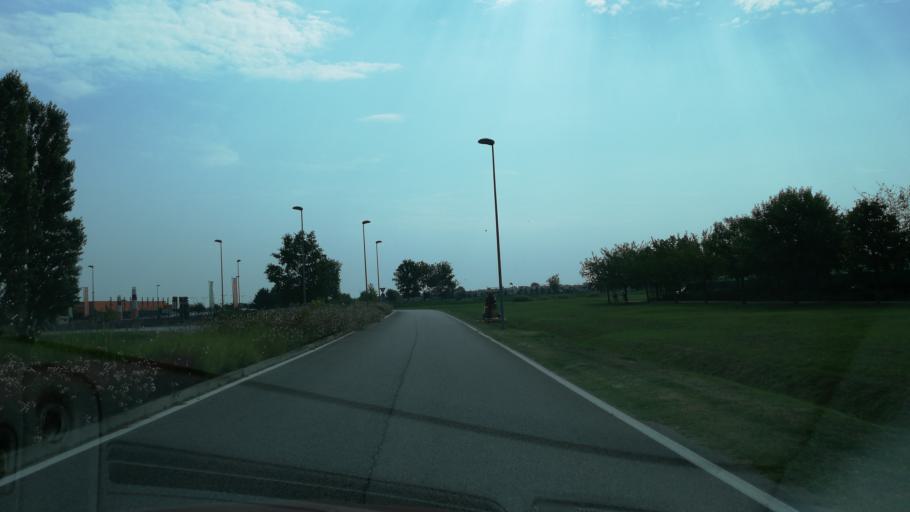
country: IT
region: Veneto
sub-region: Provincia di Venezia
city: Caorle
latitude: 45.5799
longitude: 12.8288
